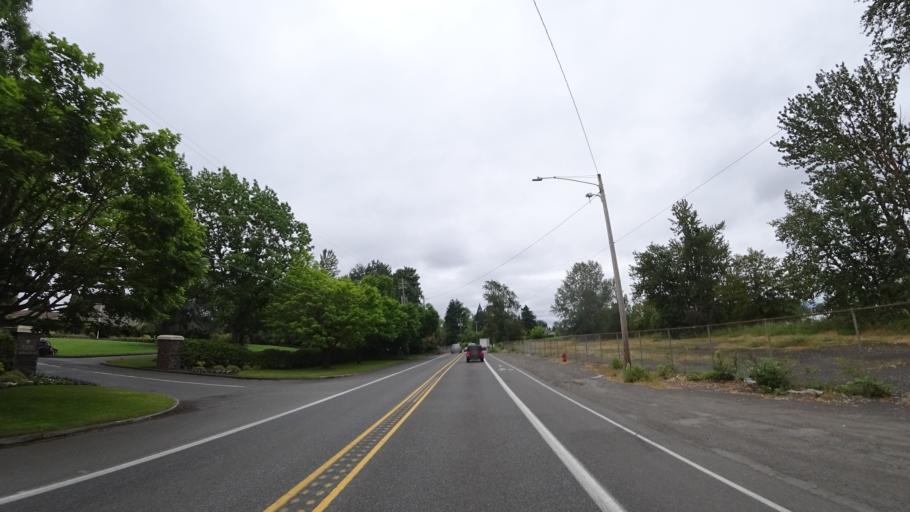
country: US
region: Washington
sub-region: Clark County
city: Vancouver
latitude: 45.6005
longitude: -122.6418
